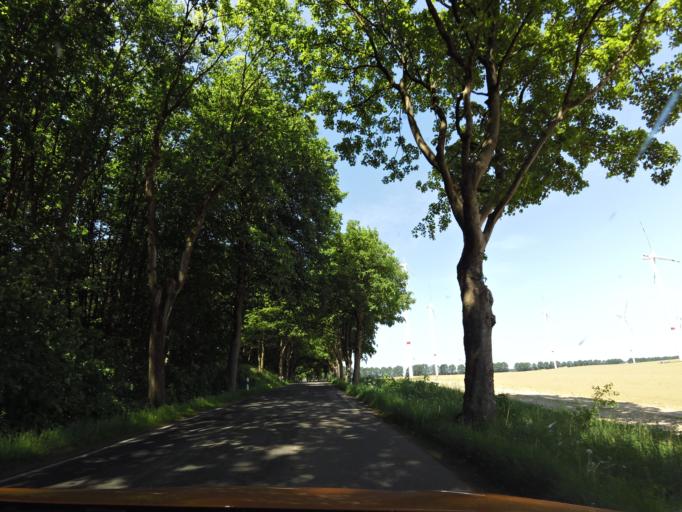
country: DE
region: Mecklenburg-Vorpommern
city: Neuburg
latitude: 53.4107
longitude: 11.8955
